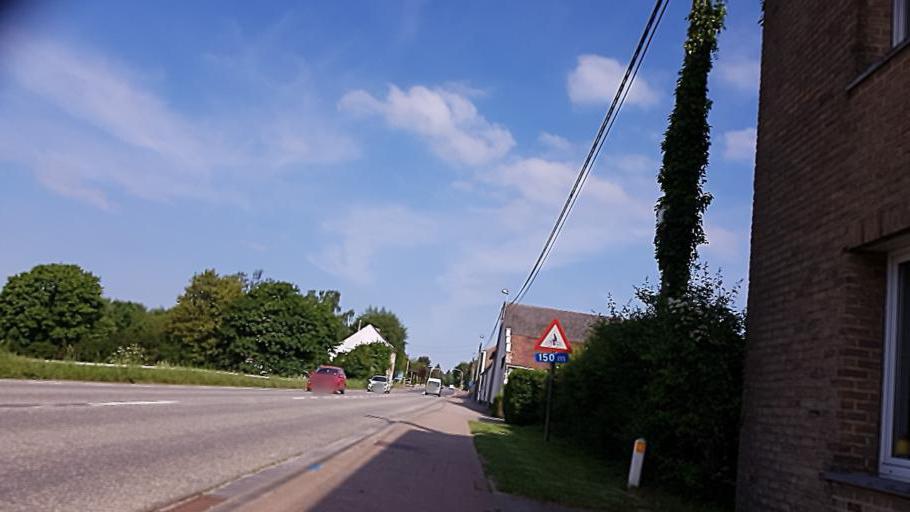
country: BE
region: Flanders
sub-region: Provincie Vlaams-Brabant
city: Overijse
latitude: 50.7636
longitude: 4.5550
